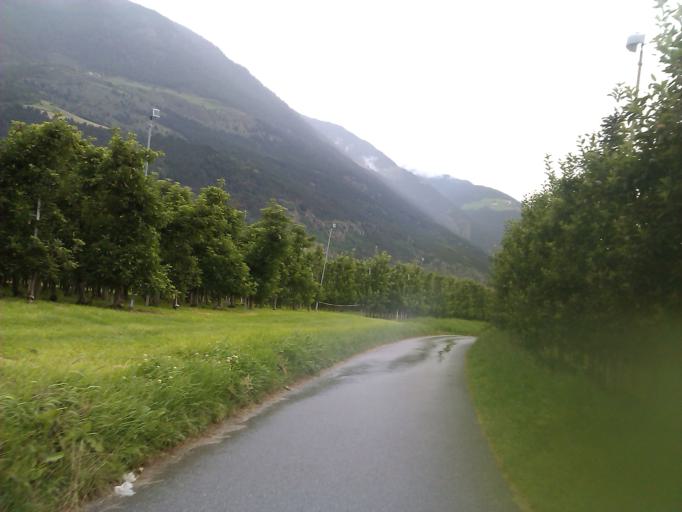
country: IT
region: Trentino-Alto Adige
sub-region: Bolzano
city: Silandro
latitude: 46.6218
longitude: 10.7717
